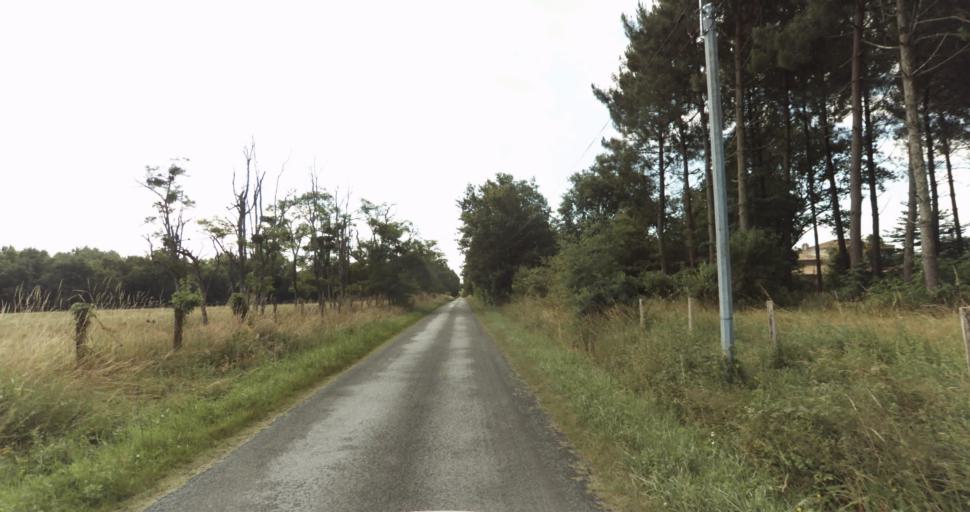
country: FR
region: Aquitaine
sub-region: Departement de la Gironde
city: Bazas
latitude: 44.4557
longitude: -0.1923
